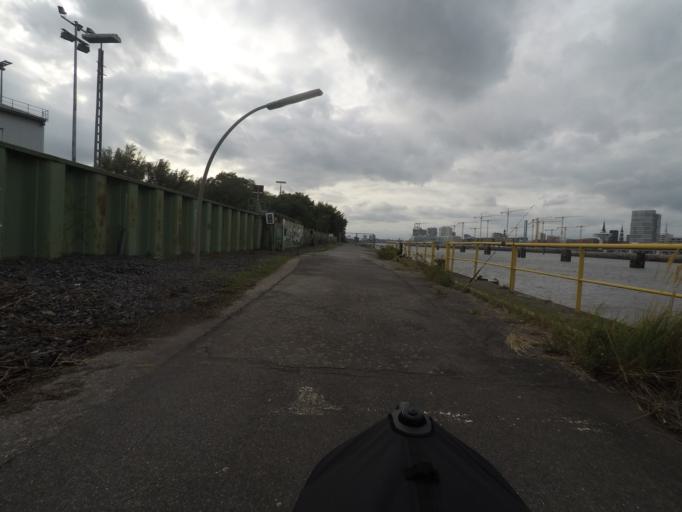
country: DE
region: Hamburg
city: Kleiner Grasbrook
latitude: 53.5347
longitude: 10.0097
